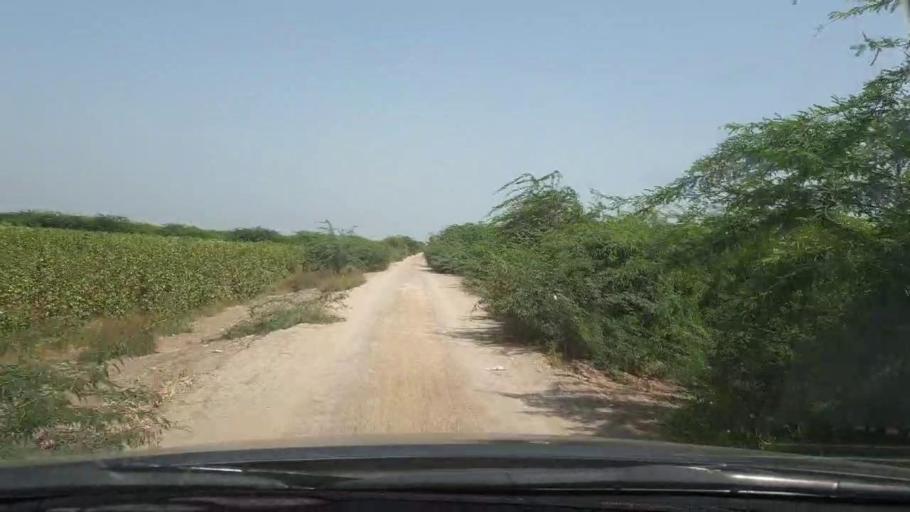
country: PK
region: Sindh
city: Naukot
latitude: 24.8132
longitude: 69.2516
